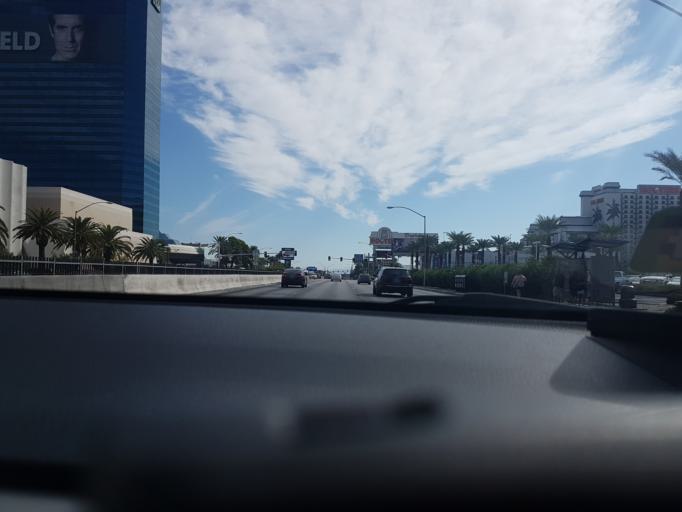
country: US
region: Nevada
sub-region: Clark County
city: Paradise
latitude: 36.1008
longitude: -115.1711
